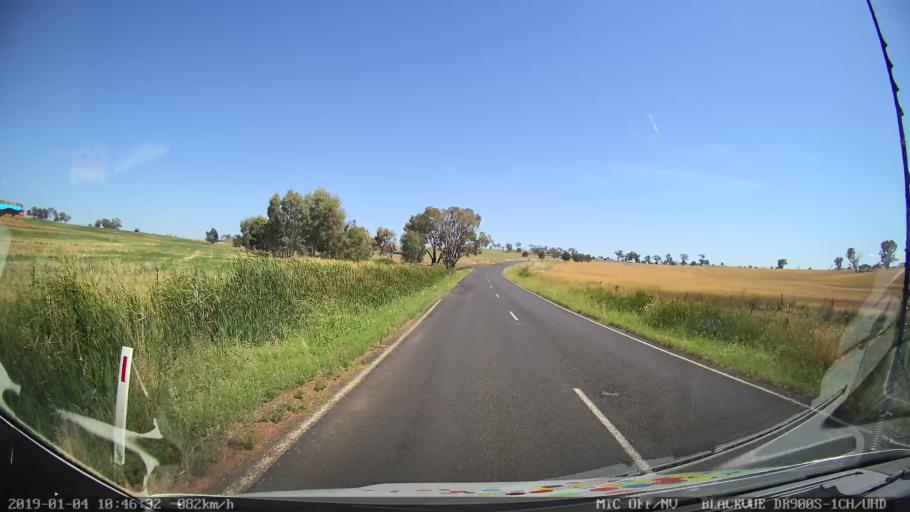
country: AU
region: New South Wales
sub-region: Cabonne
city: Molong
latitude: -33.2803
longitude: 148.7223
